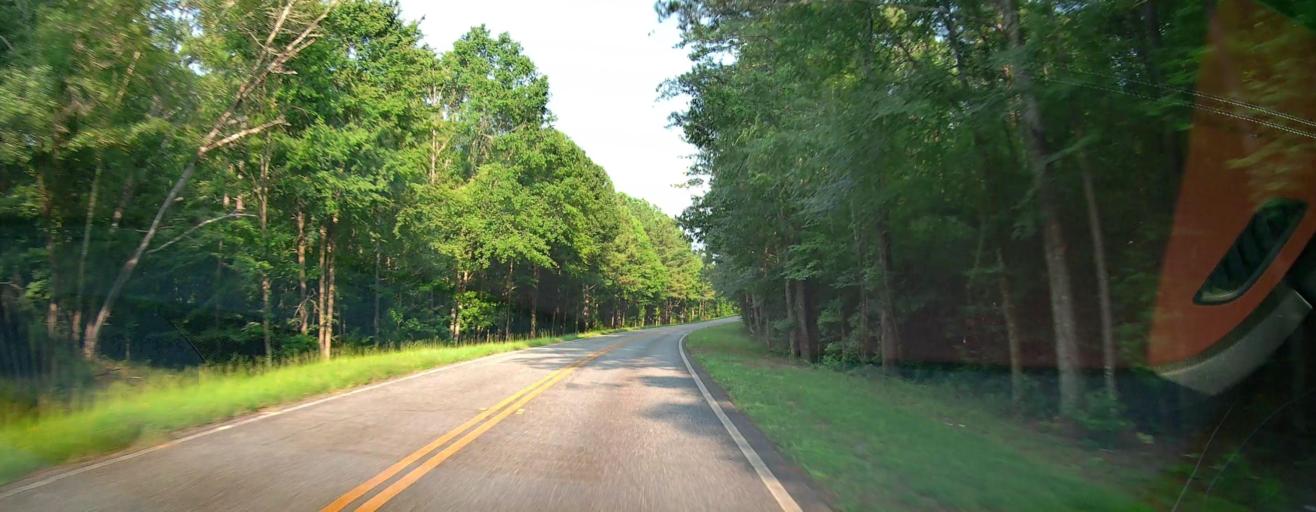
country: US
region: Georgia
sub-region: Monroe County
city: Forsyth
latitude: 33.1094
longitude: -83.7817
